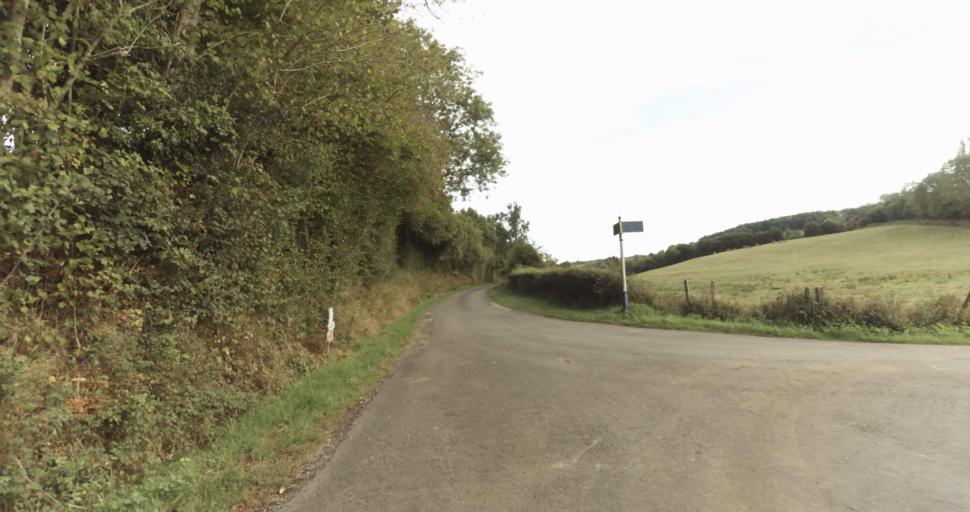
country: FR
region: Lower Normandy
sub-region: Departement de l'Orne
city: Gace
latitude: 48.8290
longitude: 0.2204
